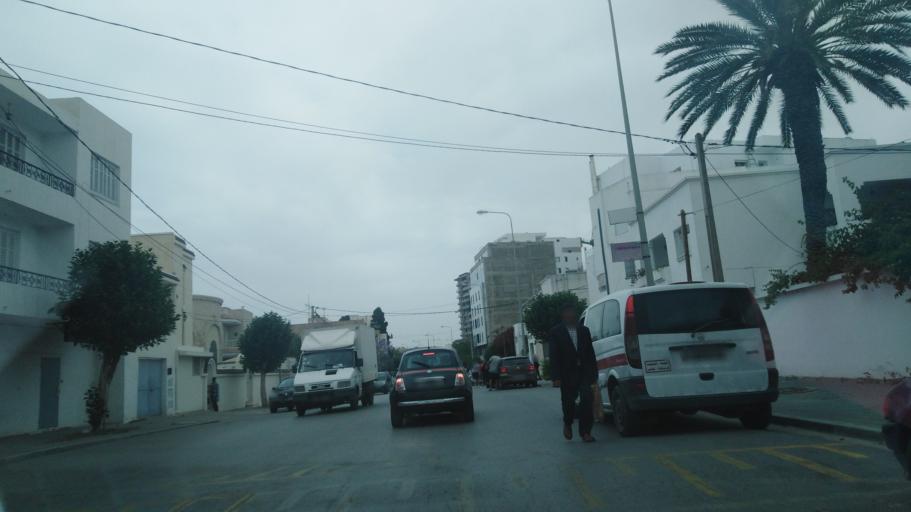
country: TN
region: Susah
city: Sousse
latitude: 35.8288
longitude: 10.6308
